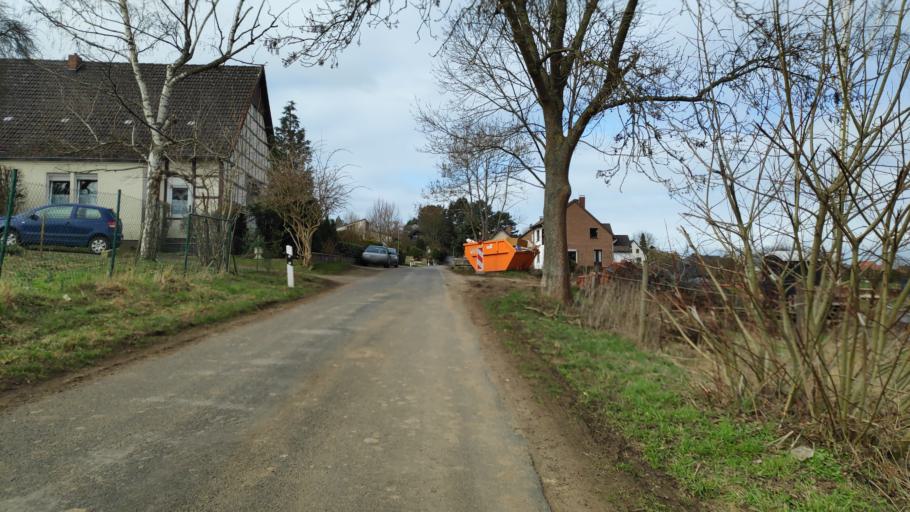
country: DE
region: North Rhine-Westphalia
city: Porta Westfalica
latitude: 52.2564
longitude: 8.8785
